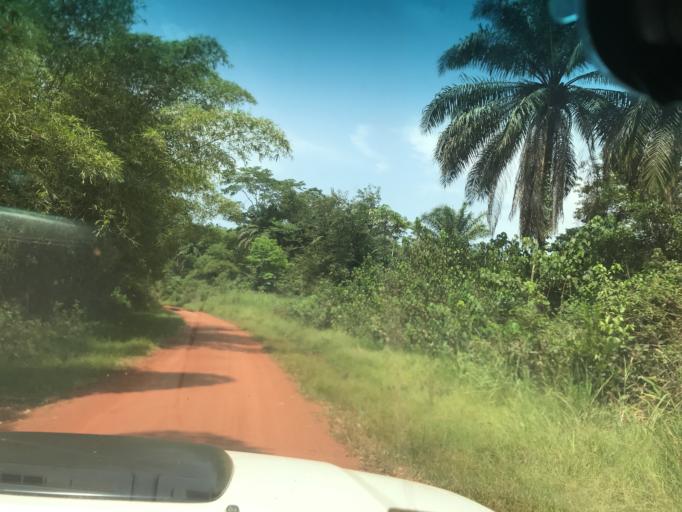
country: CD
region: Eastern Province
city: Aketi
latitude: 2.8879
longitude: 23.9787
